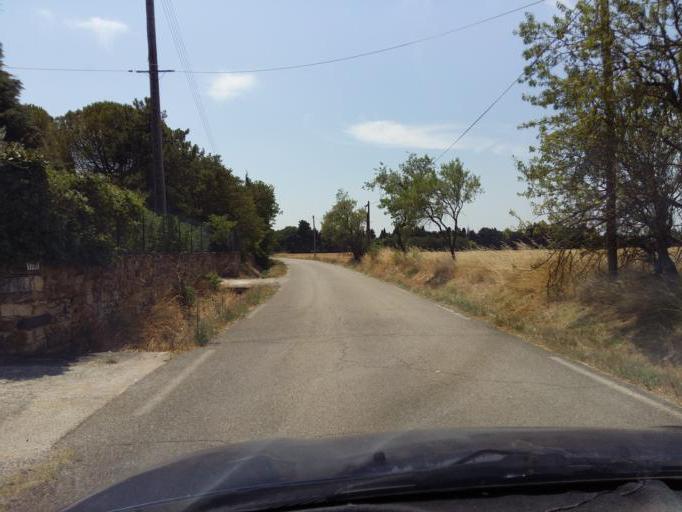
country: FR
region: Provence-Alpes-Cote d'Azur
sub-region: Departement du Vaucluse
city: Orange
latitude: 44.1561
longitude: 4.8351
